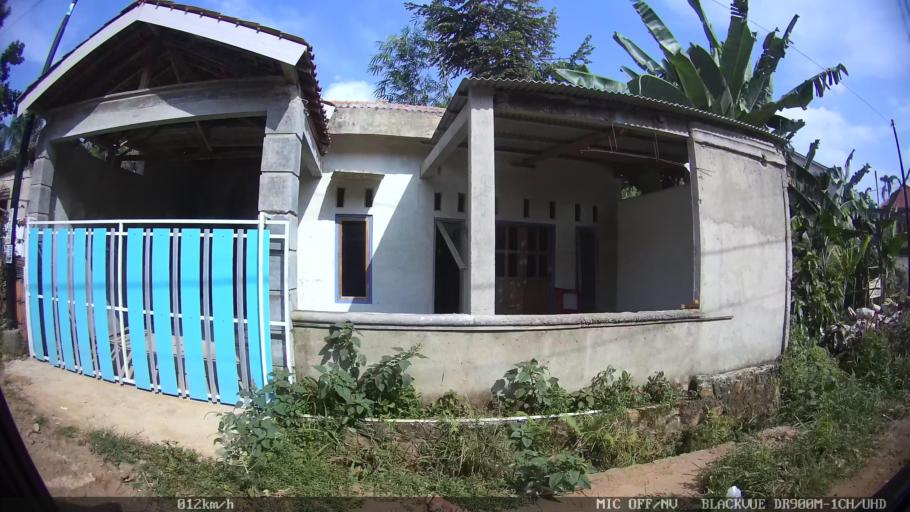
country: ID
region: Lampung
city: Kedaton
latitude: -5.3873
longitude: 105.2297
